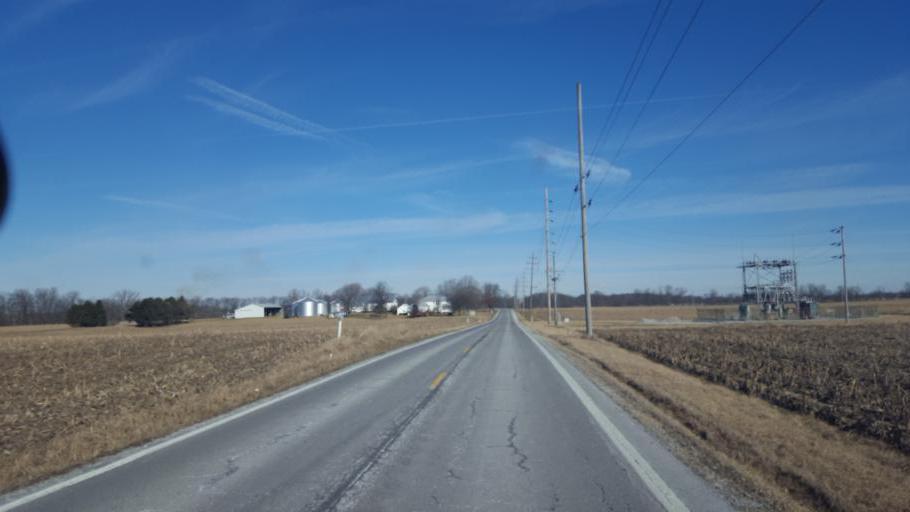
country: US
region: Ohio
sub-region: Marion County
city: Marion
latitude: 40.5384
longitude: -83.1896
